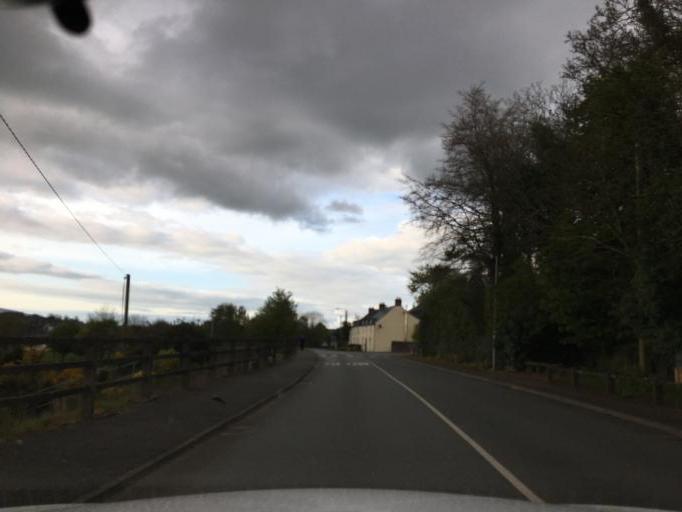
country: IE
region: Leinster
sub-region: Loch Garman
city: New Ross
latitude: 52.3885
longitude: -6.9496
